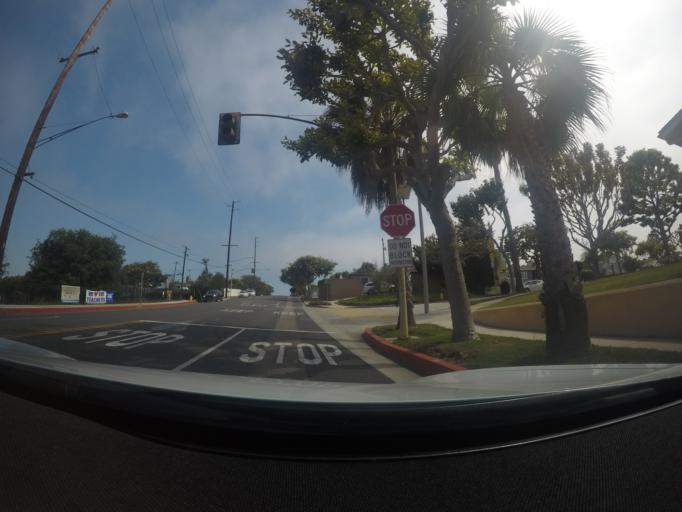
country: US
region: California
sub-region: Los Angeles County
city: Palos Verdes Estates
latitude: 33.8202
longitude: -118.3770
